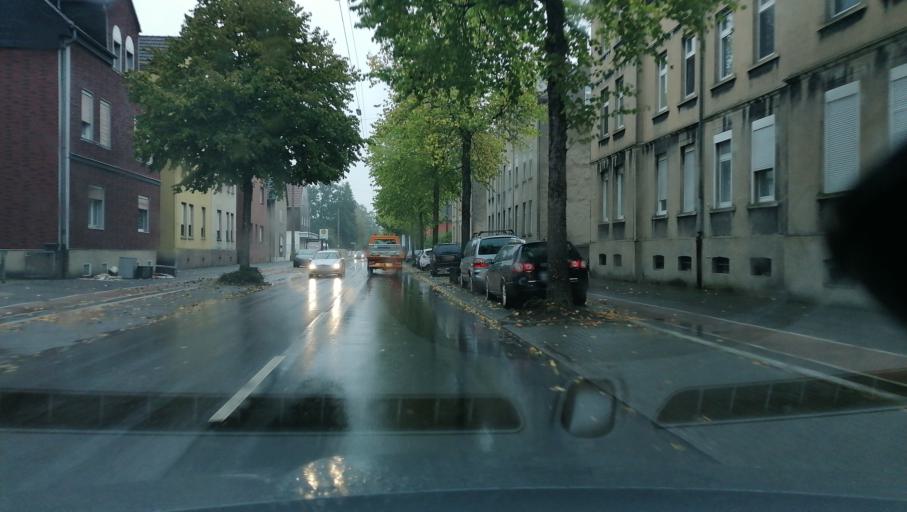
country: DE
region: North Rhine-Westphalia
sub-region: Regierungsbezirk Arnsberg
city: Herne
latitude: 51.5761
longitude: 7.2446
